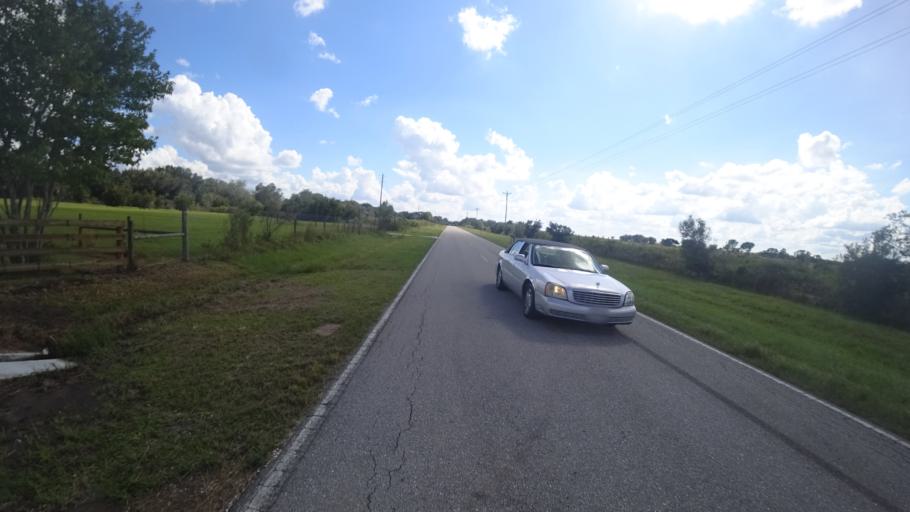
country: US
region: Florida
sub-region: Sarasota County
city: Lake Sarasota
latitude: 27.4135
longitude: -82.1333
